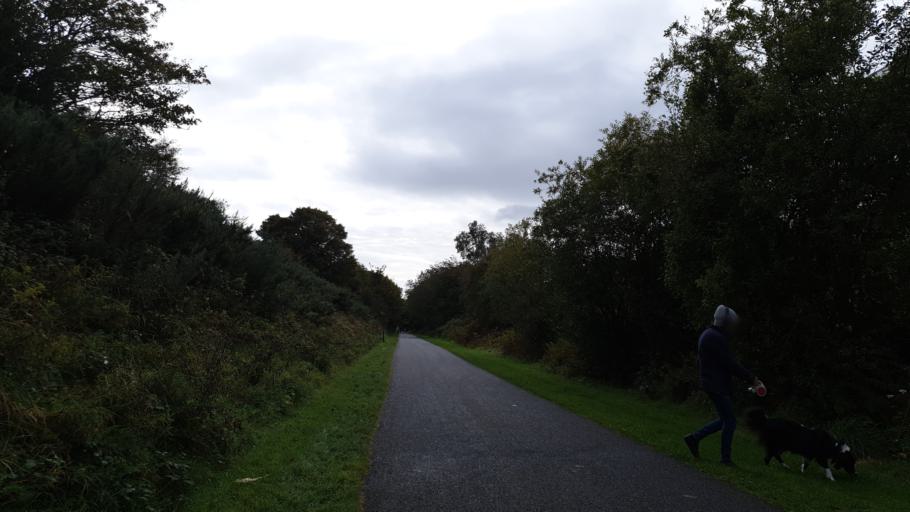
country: IE
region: Munster
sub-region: County Cork
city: Cork
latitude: 51.8927
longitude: -8.4144
